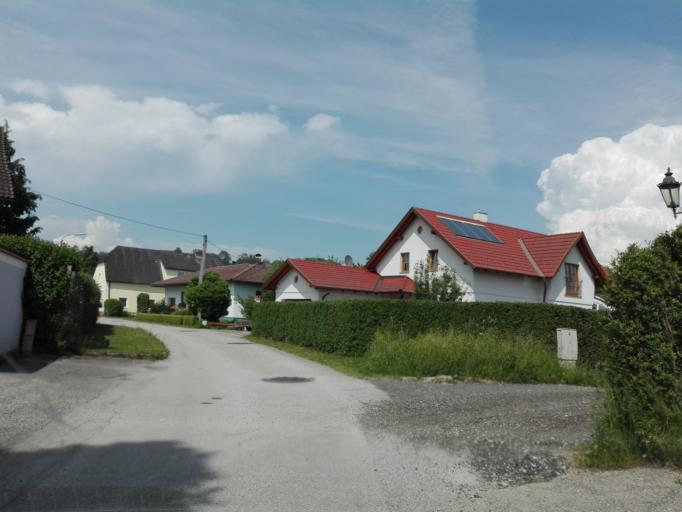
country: AT
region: Upper Austria
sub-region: Politischer Bezirk Perg
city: Perg
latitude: 48.2301
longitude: 14.6879
